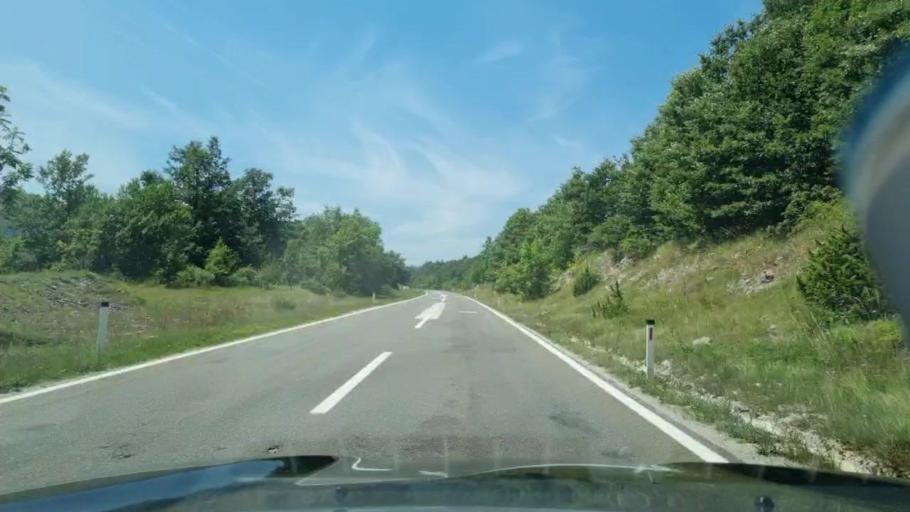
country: BA
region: Federation of Bosnia and Herzegovina
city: Sanica
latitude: 44.5557
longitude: 16.5331
